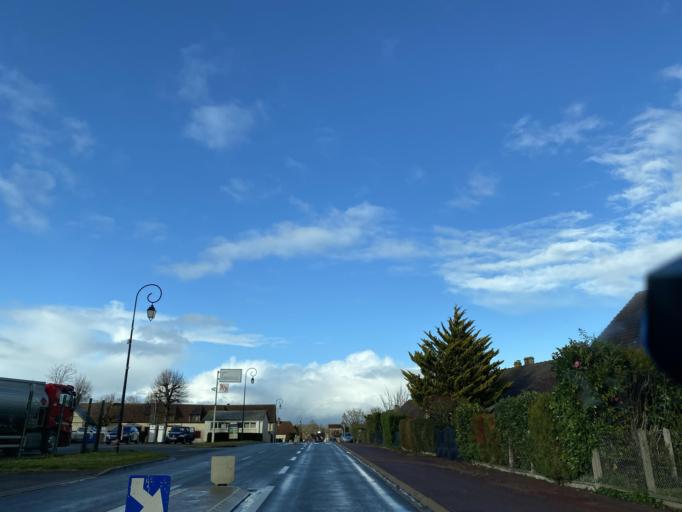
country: FR
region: Centre
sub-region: Departement d'Eure-et-Loir
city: Chateauneuf-en-Thymerais
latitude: 48.6254
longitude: 1.1507
